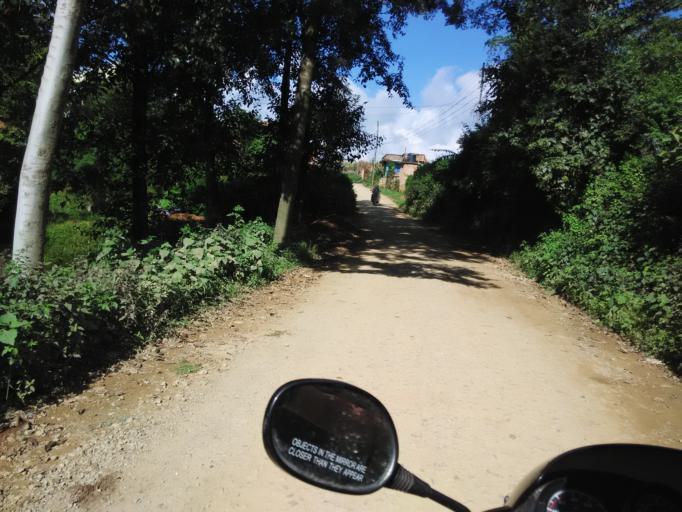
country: NP
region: Central Region
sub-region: Bagmati Zone
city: Patan
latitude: 27.6072
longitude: 85.3411
